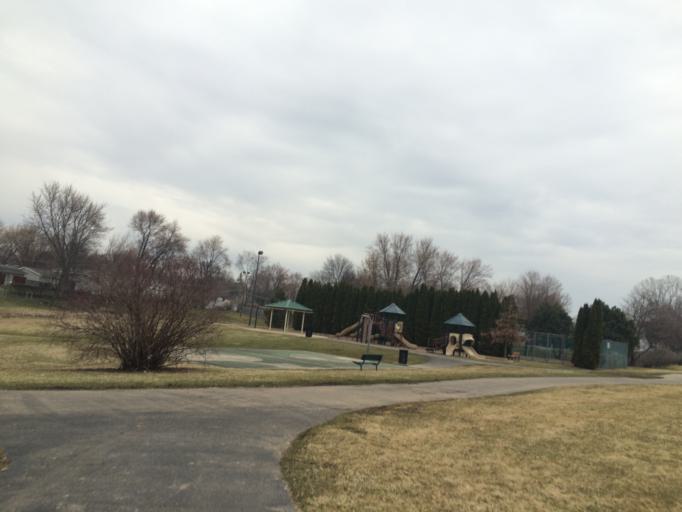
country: US
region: Illinois
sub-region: DuPage County
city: Hanover Park
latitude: 42.0103
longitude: -88.1430
